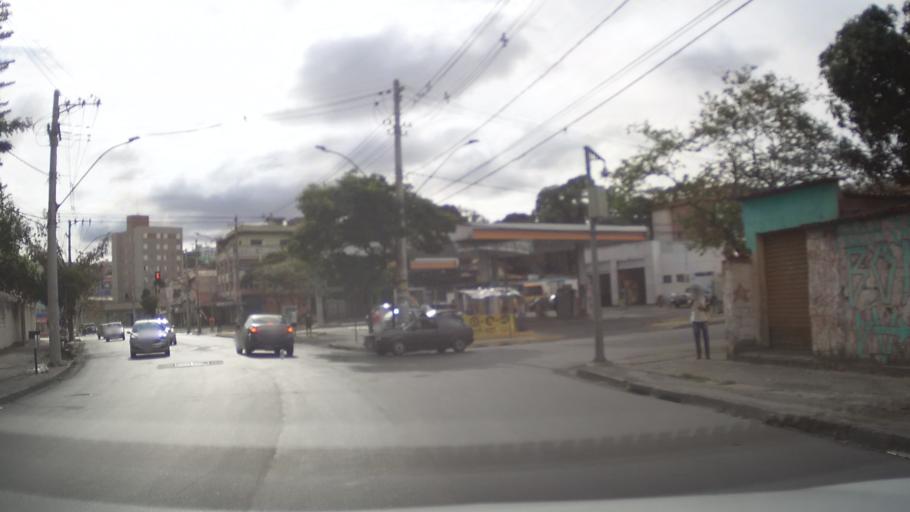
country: BR
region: Minas Gerais
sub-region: Belo Horizonte
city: Belo Horizonte
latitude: -19.8287
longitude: -43.9646
